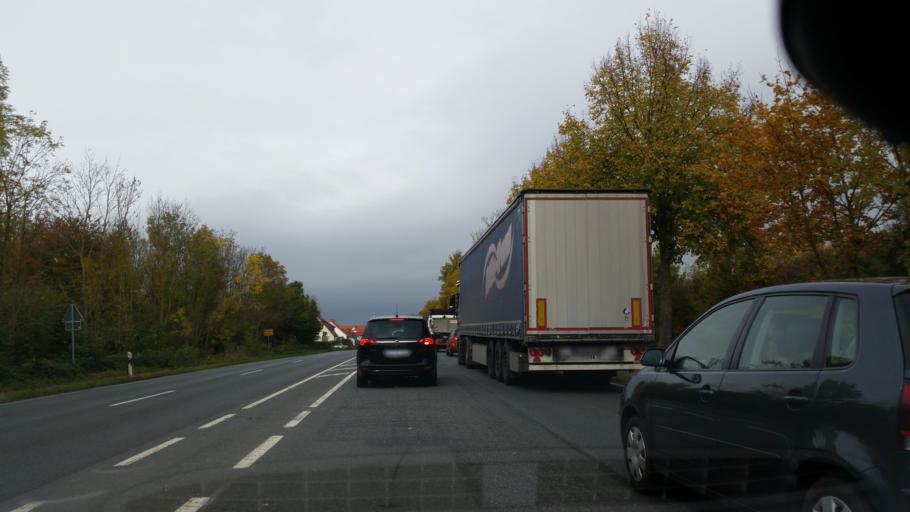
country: DE
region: Lower Saxony
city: Giesen
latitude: 52.1910
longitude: 9.9234
